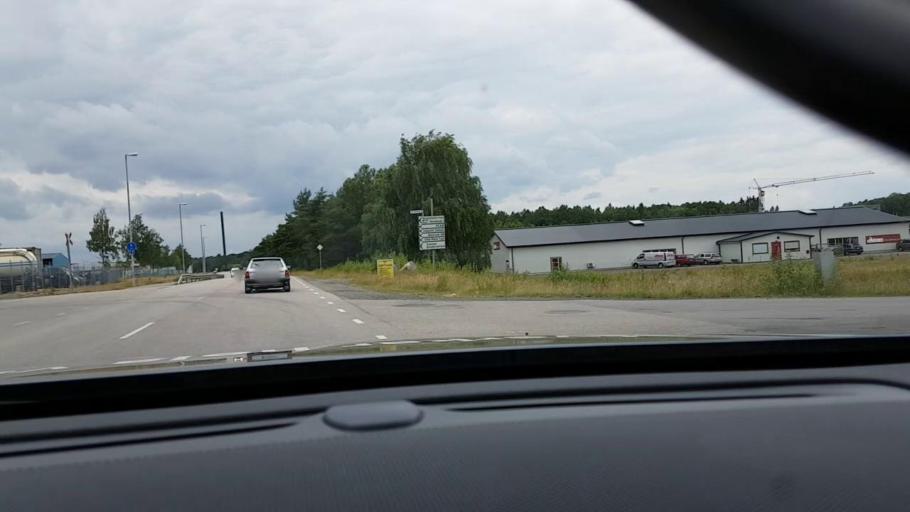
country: SE
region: Skane
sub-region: Hassleholms Kommun
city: Hassleholm
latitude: 56.1570
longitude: 13.8119
